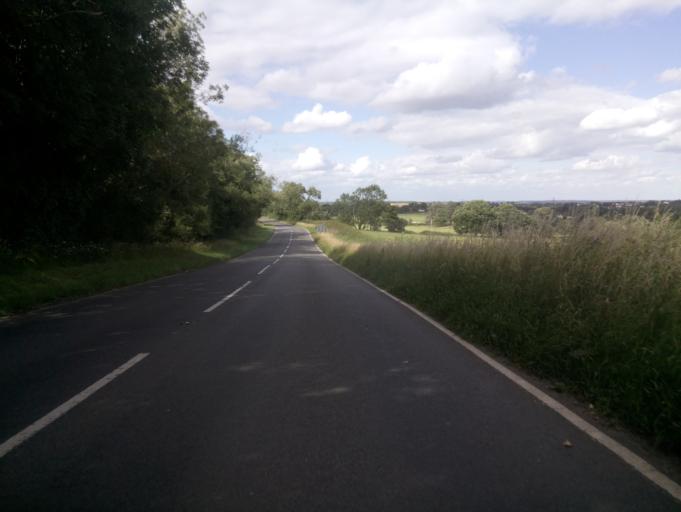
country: GB
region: England
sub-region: Leicestershire
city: Coalville
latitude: 52.7527
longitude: -1.4160
